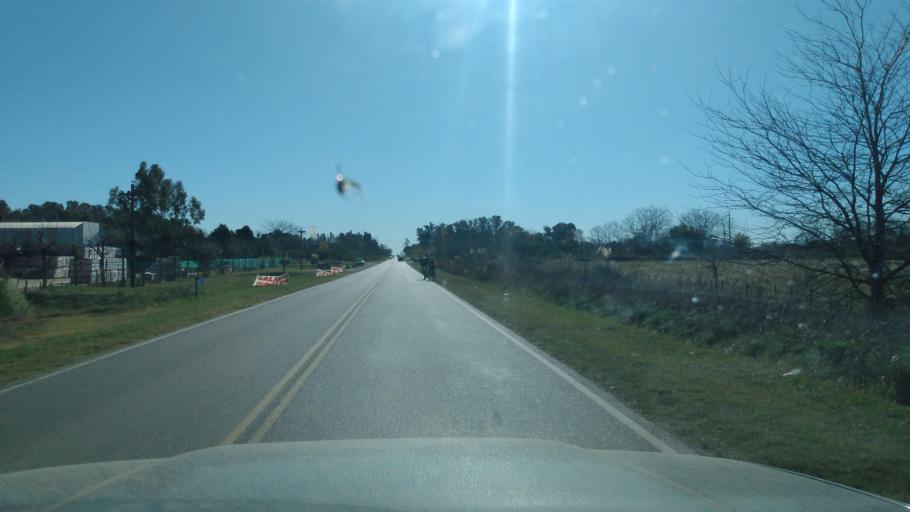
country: AR
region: Buenos Aires
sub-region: Partido de Lujan
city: Lujan
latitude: -34.5252
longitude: -59.1721
